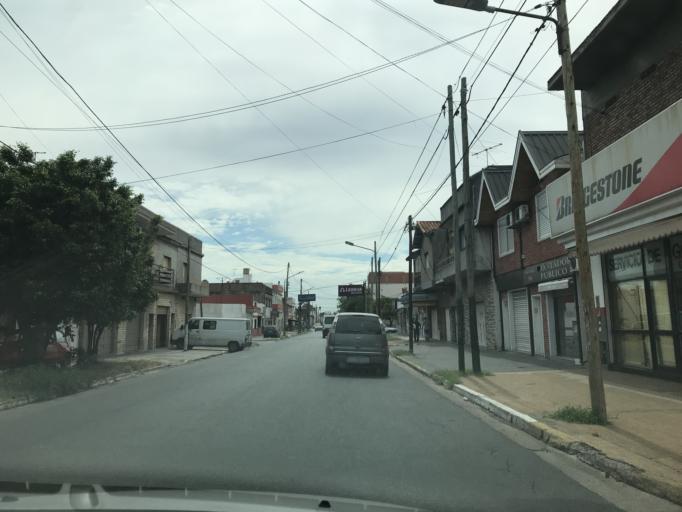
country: AR
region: Buenos Aires
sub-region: Partido de Lomas de Zamora
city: Lomas de Zamora
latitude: -34.7302
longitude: -58.4240
